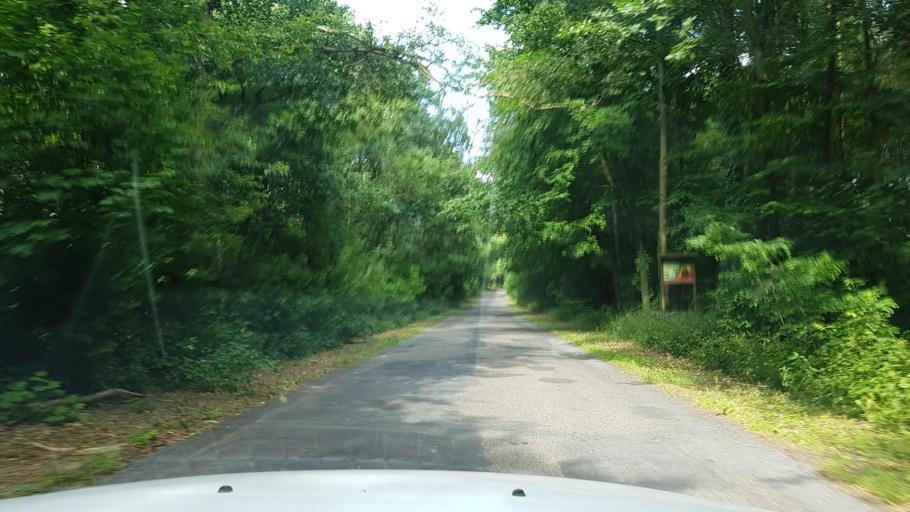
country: PL
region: West Pomeranian Voivodeship
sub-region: Powiat goleniowski
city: Mosty
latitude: 53.5495
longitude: 14.9594
